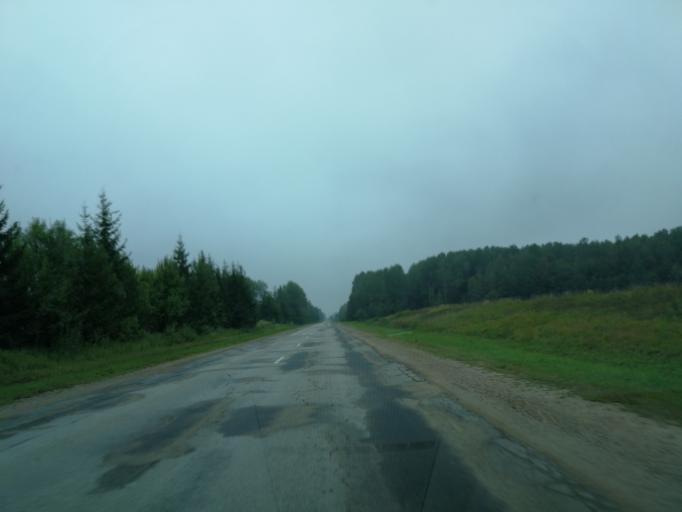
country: LV
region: Varkava
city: Vecvarkava
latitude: 56.3165
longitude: 26.4804
